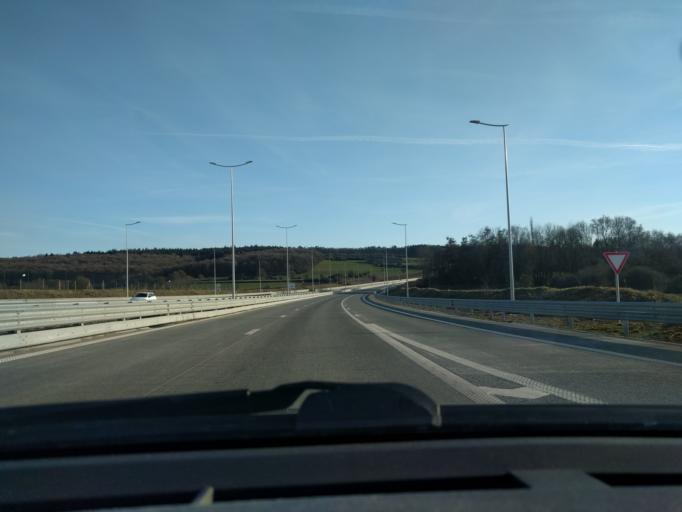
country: BE
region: Wallonia
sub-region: Province de Namur
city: Couvin
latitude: 50.0523
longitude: 4.5102
